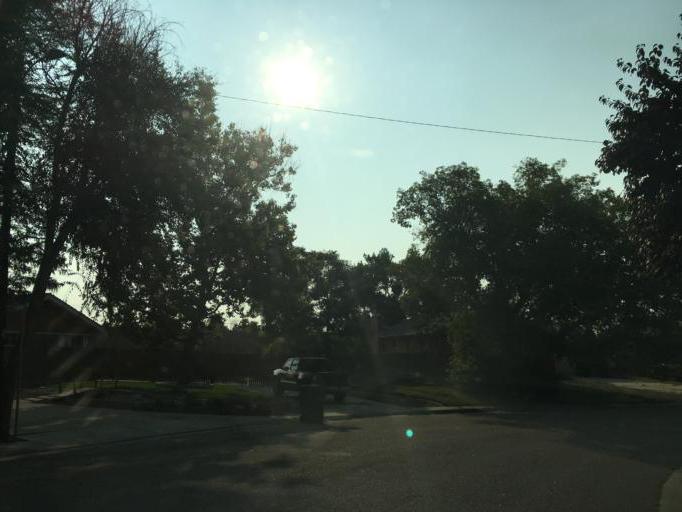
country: US
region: Colorado
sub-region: Adams County
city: Northglenn
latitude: 39.8798
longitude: -104.9888
